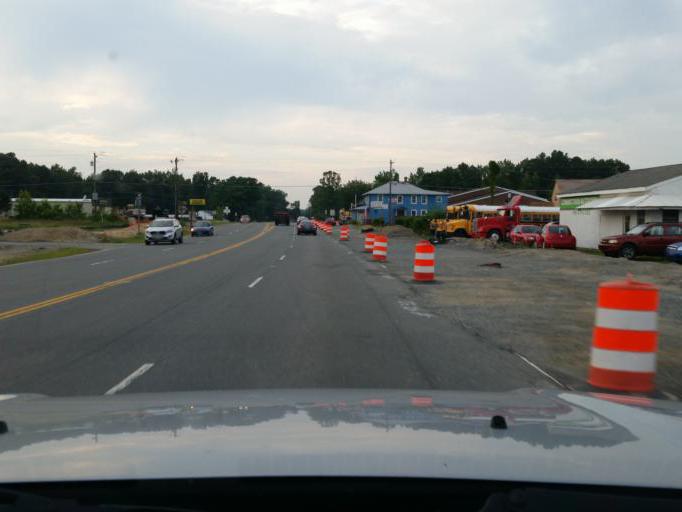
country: US
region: Virginia
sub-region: Spotsylvania County
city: Spotsylvania Courthouse
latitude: 38.1340
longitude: -77.5215
